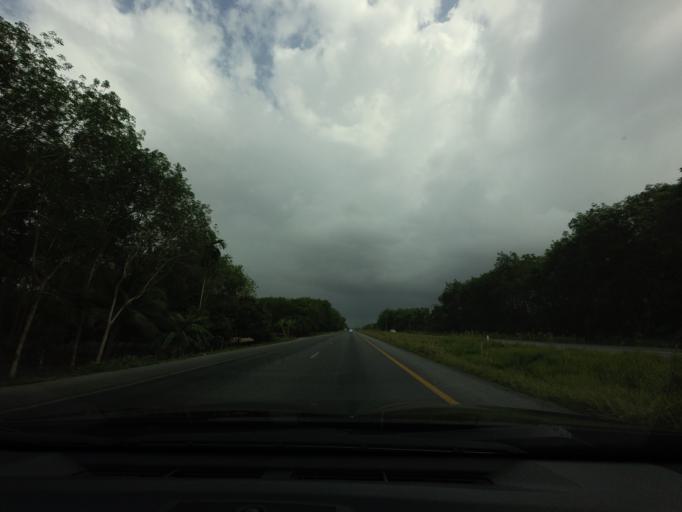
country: TH
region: Pattani
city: Mae Lan
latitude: 6.7132
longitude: 101.2279
